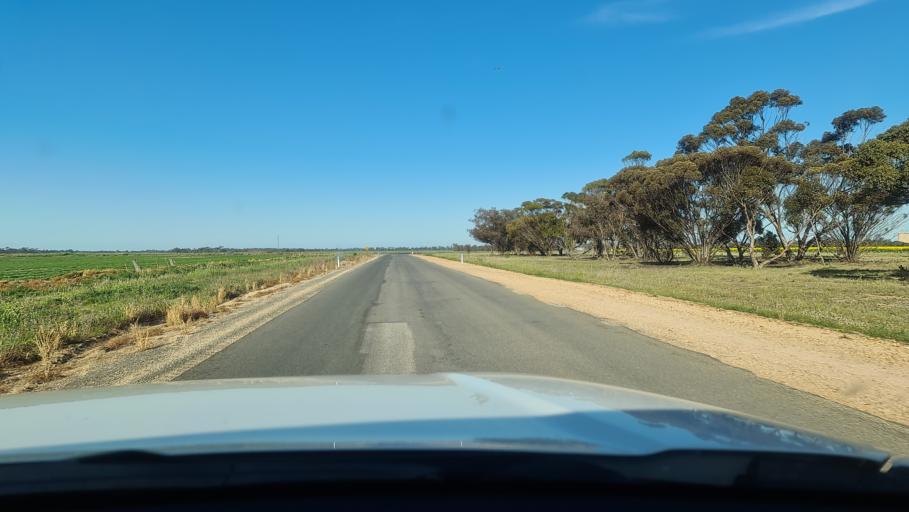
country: AU
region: Victoria
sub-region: Horsham
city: Horsham
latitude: -36.4493
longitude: 142.5673
